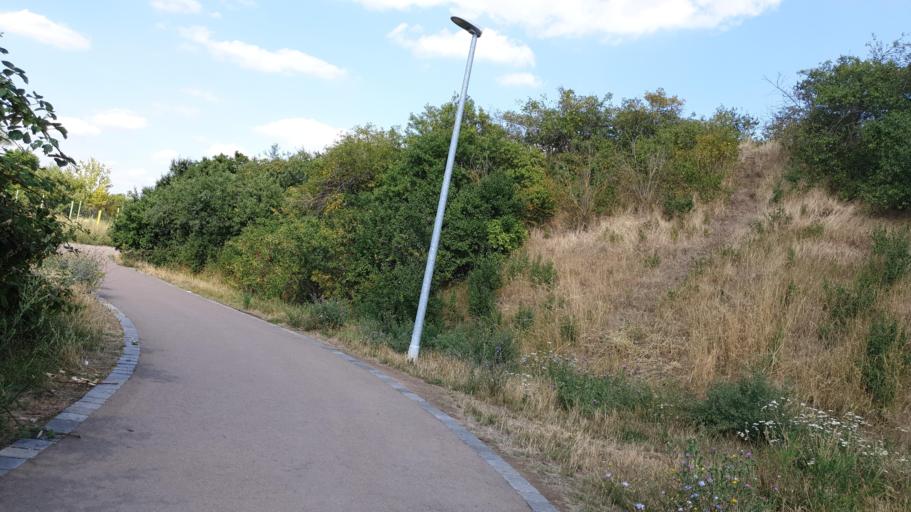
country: DE
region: Saxony-Anhalt
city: Bernburg
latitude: 51.7833
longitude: 11.7578
